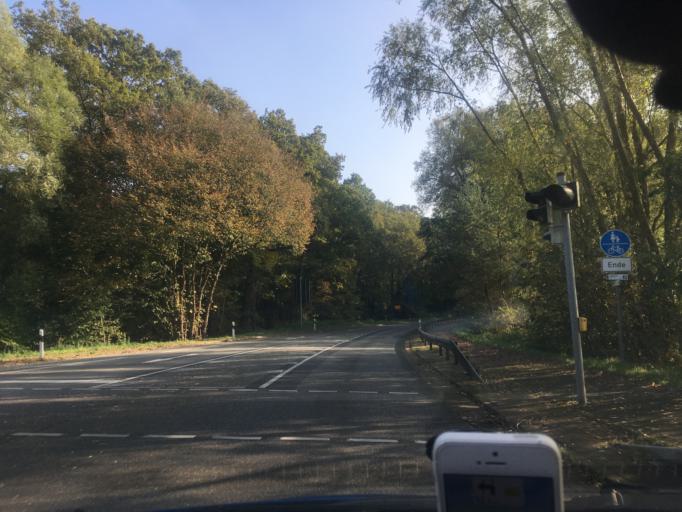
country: DE
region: Mecklenburg-Vorpommern
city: Boizenburg
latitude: 53.3941
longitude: 10.8125
